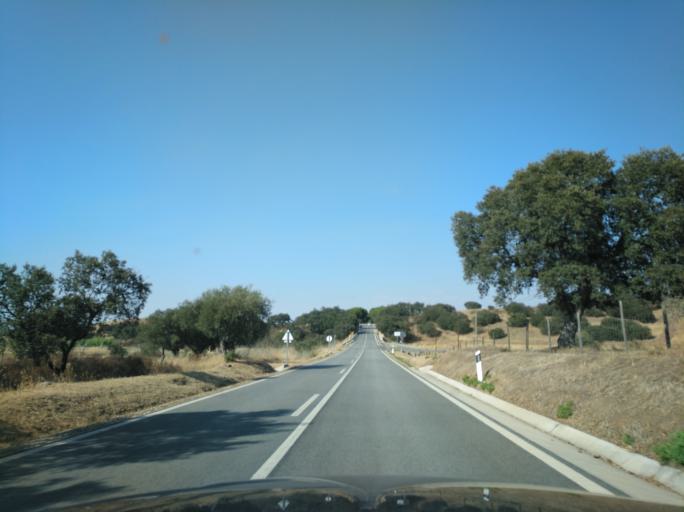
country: ES
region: Andalusia
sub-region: Provincia de Huelva
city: Rosal de la Frontera
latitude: 38.0321
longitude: -7.2695
